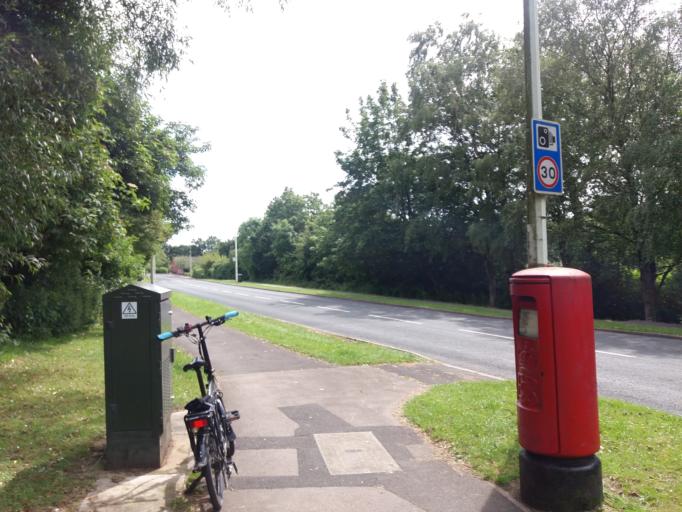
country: GB
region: England
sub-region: Lancashire
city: Clayton-le-Woods
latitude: 53.7039
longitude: -2.6455
